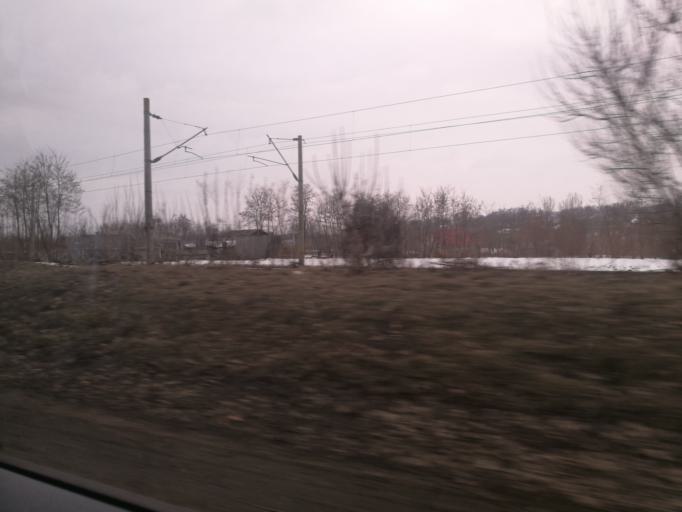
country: RO
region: Iasi
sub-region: Comuna Ruginoasa
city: Rediu
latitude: 47.2472
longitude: 26.8591
